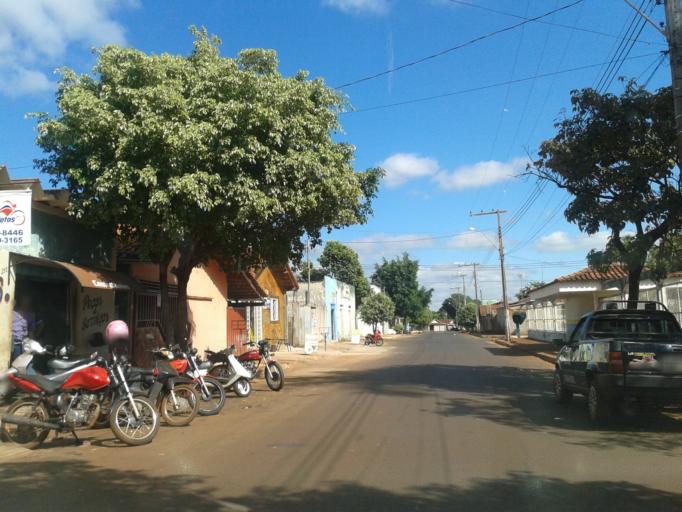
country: BR
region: Minas Gerais
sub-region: Centralina
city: Centralina
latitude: -18.5812
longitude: -49.2033
